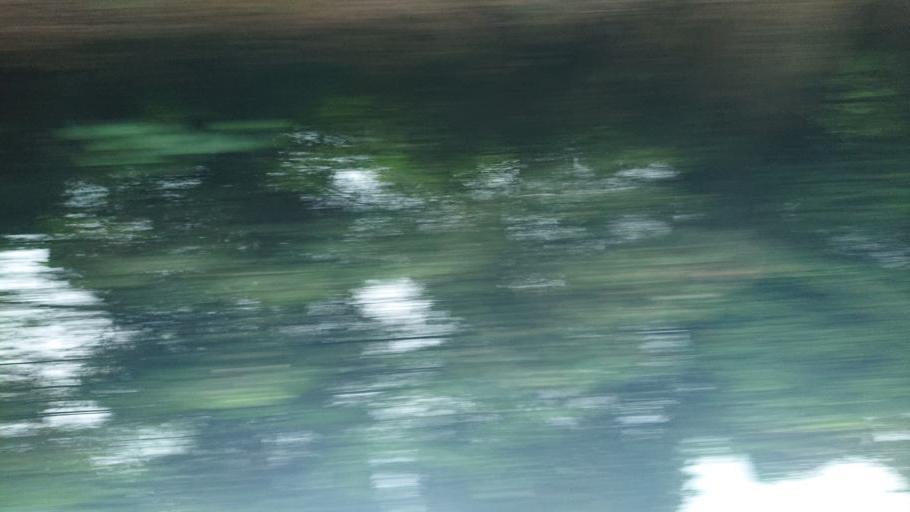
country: TW
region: Taiwan
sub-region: Chiayi
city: Jiayi Shi
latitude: 23.4780
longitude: 120.7164
